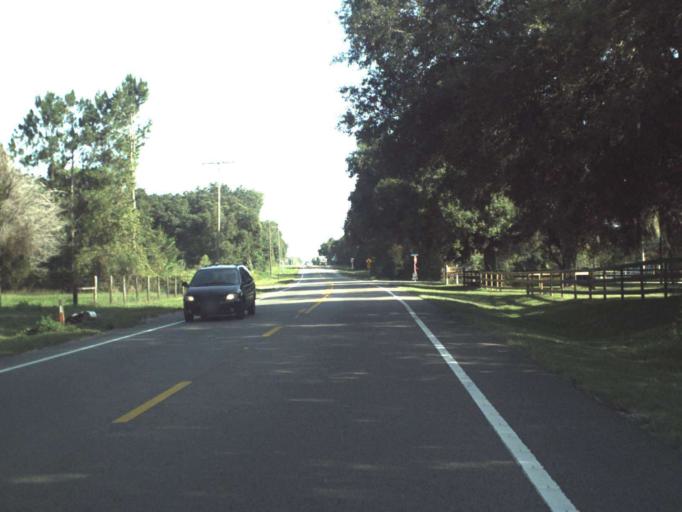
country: US
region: Florida
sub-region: Lake County
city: Groveland
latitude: 28.4124
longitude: -81.8309
